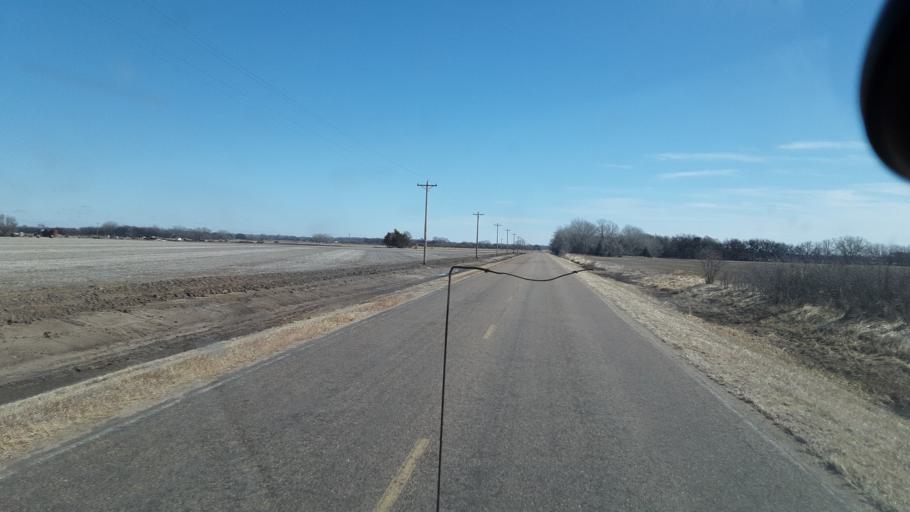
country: US
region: Kansas
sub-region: Reno County
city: Nickerson
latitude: 38.2174
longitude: -98.0833
